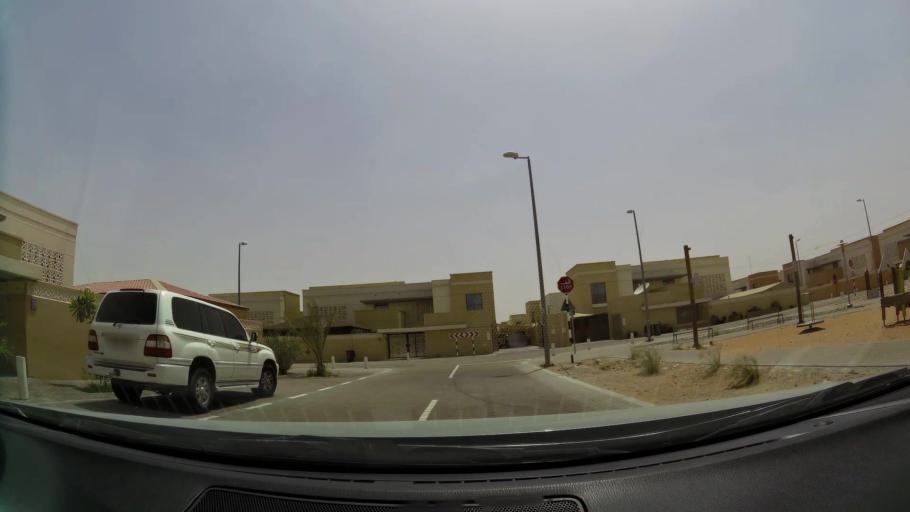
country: AE
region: Abu Dhabi
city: Al Ain
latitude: 24.1475
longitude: 55.6256
